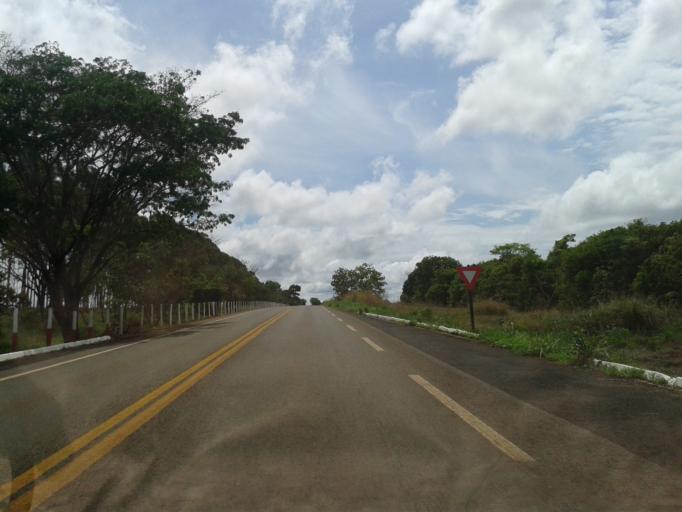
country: BR
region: Goias
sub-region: Buriti Alegre
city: Buriti Alegre
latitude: -18.1335
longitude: -49.0729
